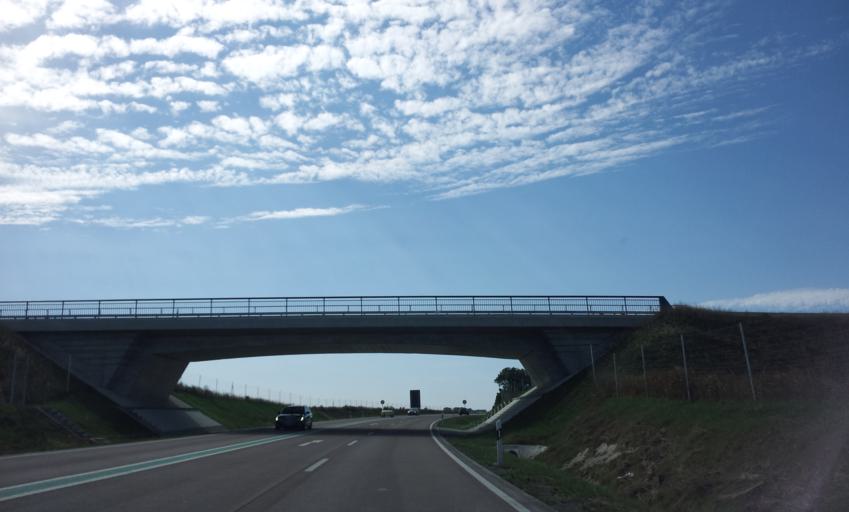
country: DE
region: Mecklenburg-Vorpommern
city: Samtens
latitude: 54.3493
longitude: 13.2903
